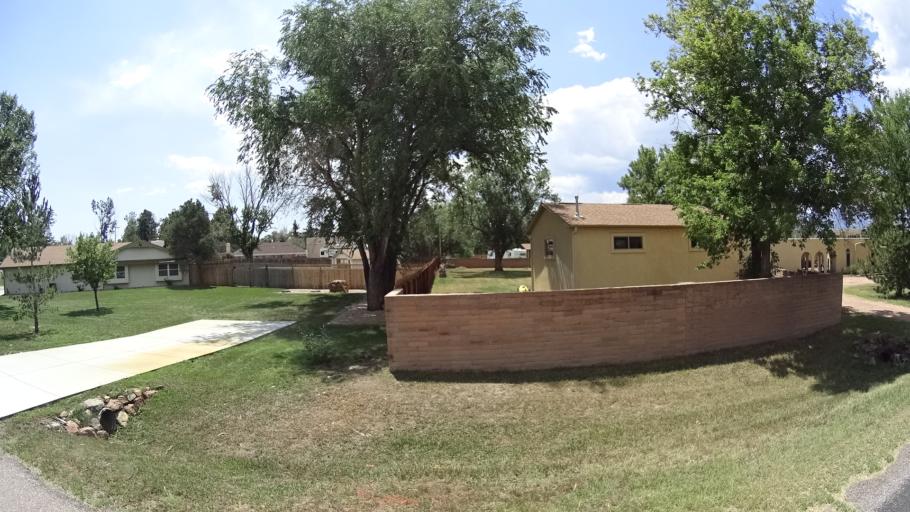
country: US
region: Colorado
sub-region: El Paso County
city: Air Force Academy
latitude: 38.9383
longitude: -104.8098
